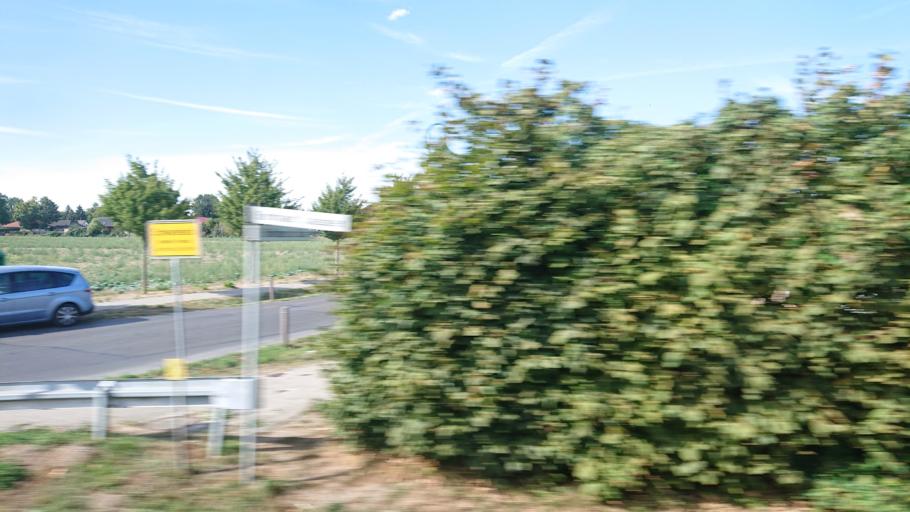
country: DE
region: Brandenburg
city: Bernau bei Berlin
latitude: 52.6411
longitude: 13.5620
